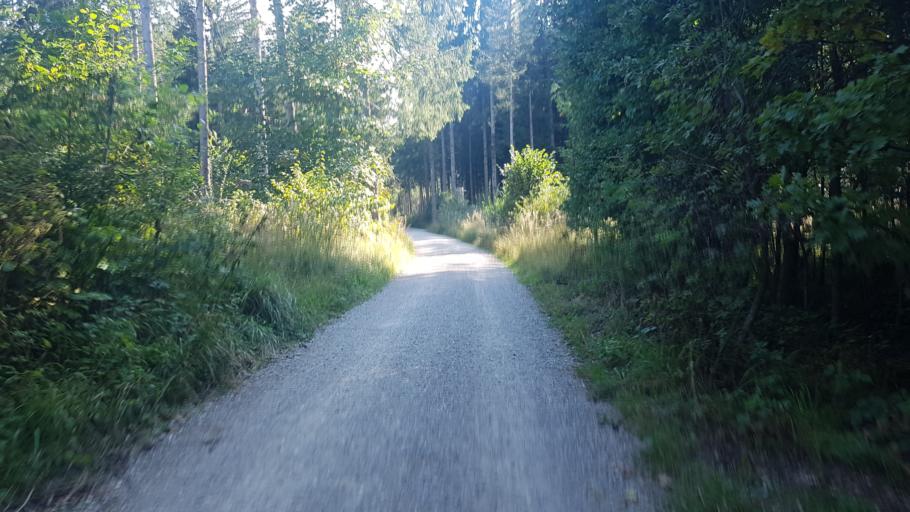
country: DE
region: Bavaria
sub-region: Upper Bavaria
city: Gilching
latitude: 48.0876
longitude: 11.3030
